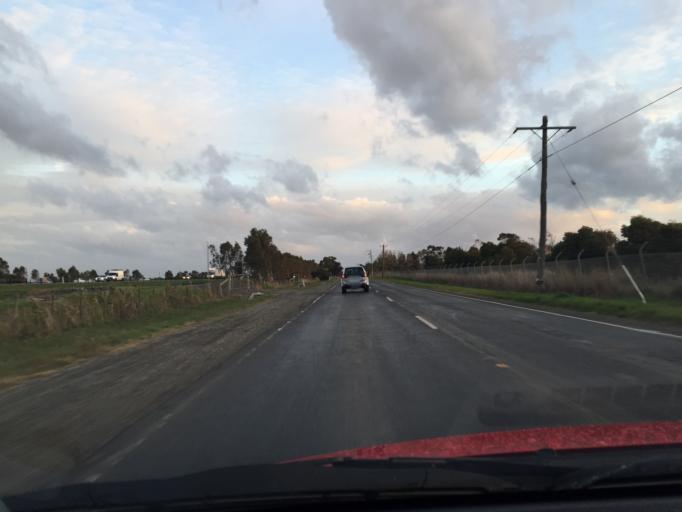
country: AU
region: Victoria
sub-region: Frankston
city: Sandhurst
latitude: -38.0472
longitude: 145.1856
